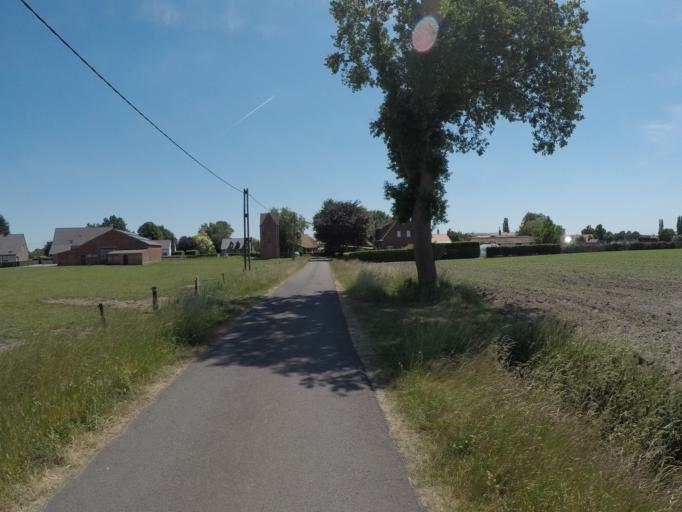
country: BE
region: Flanders
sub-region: Provincie Antwerpen
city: Wuustwezel
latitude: 51.3815
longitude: 4.5592
